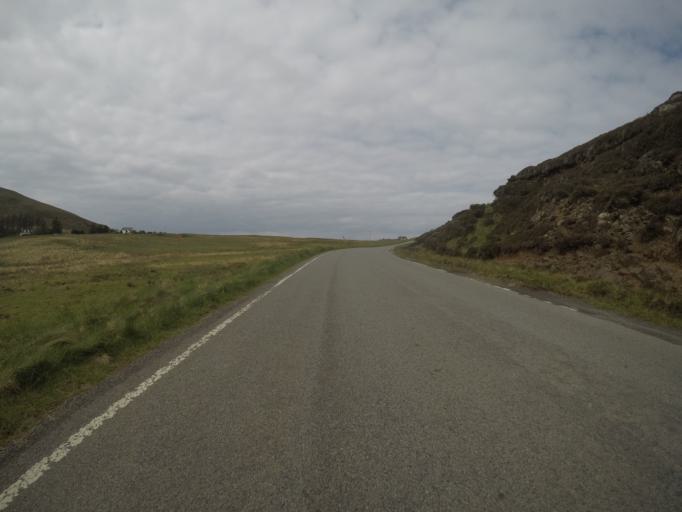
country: GB
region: Scotland
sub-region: Highland
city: Portree
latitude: 57.6829
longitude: -6.3249
